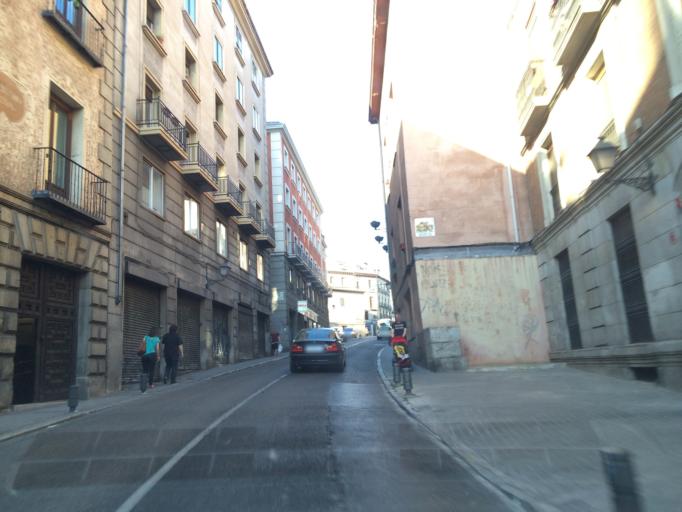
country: ES
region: Madrid
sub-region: Provincia de Madrid
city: Madrid
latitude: 40.4135
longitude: -3.7100
